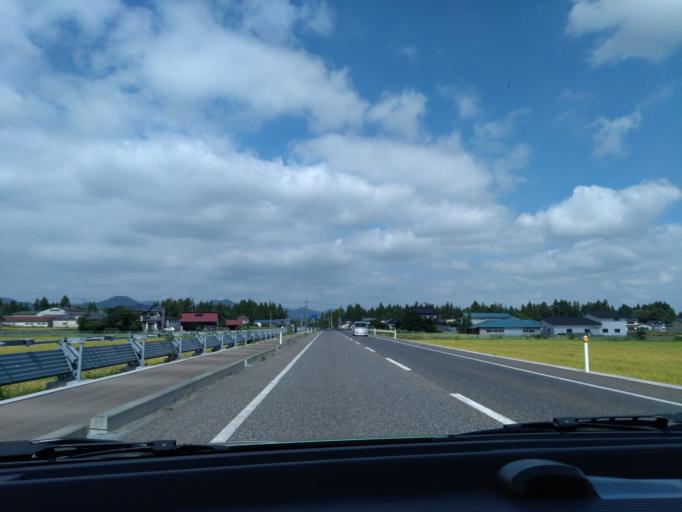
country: JP
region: Iwate
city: Hanamaki
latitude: 39.3707
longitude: 141.0569
